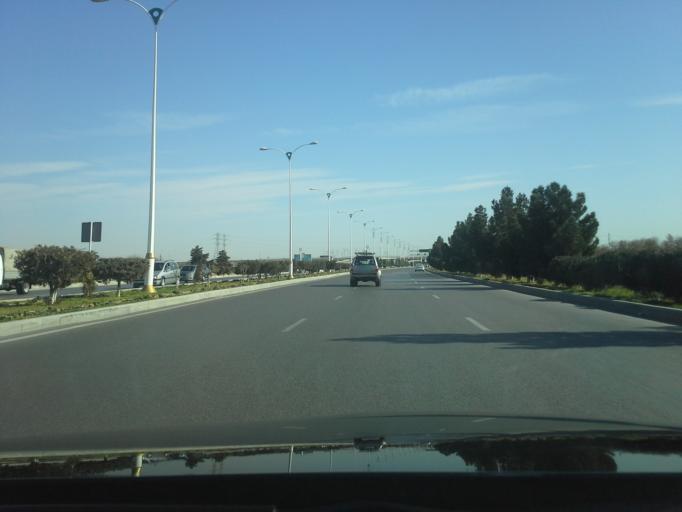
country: TM
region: Ahal
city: Annau
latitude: 37.9152
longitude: 58.4765
